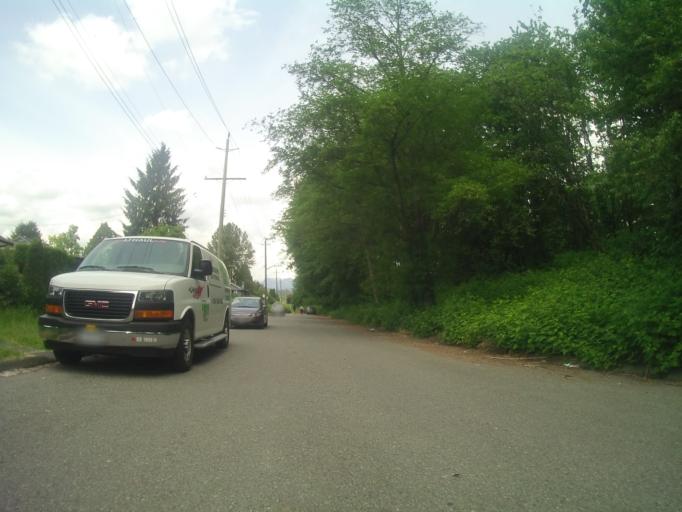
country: CA
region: British Columbia
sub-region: Fraser Valley Regional District
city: North Vancouver
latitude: 49.3063
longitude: -123.0297
